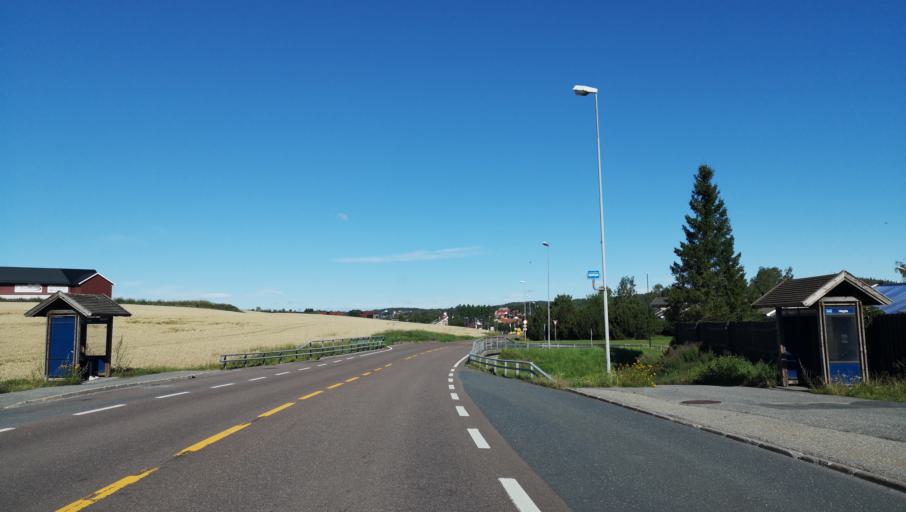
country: NO
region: Ostfold
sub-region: Spydeberg
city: Spydeberg
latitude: 59.6122
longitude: 11.0864
